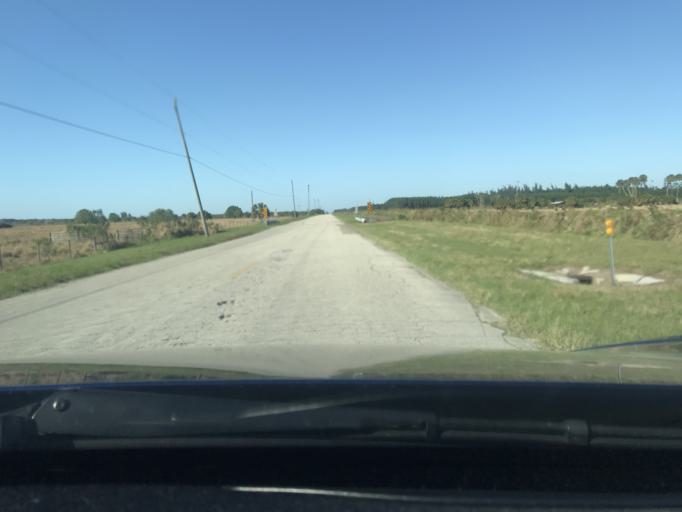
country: US
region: Florida
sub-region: Saint Lucie County
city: Fort Pierce South
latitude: 27.3923
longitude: -80.4976
